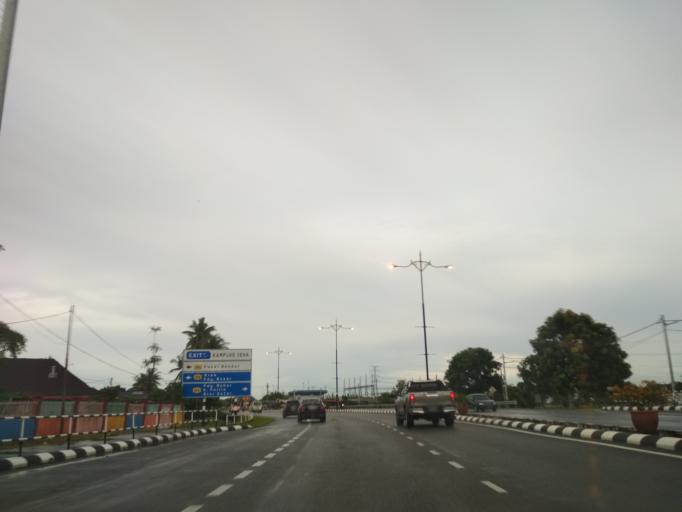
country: MY
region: Perlis
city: Kangar
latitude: 6.4377
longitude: 100.2075
